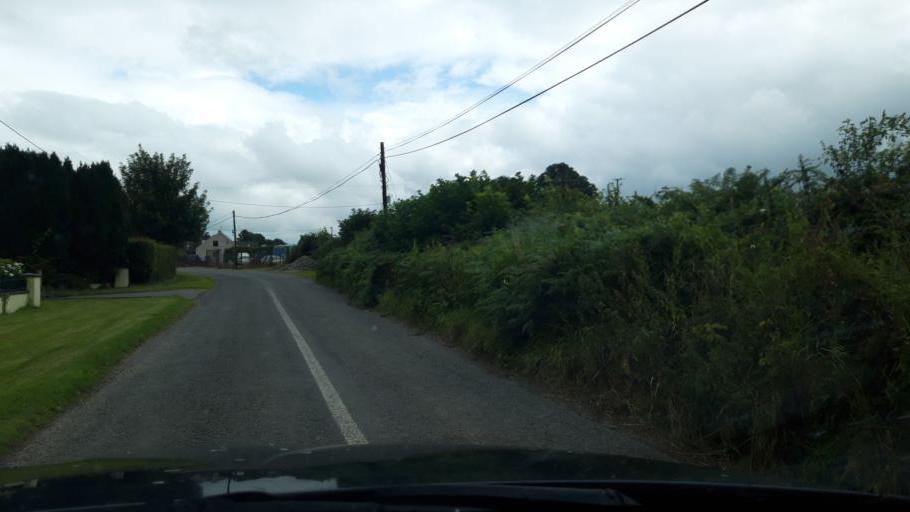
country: IE
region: Munster
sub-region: County Cork
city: Castlemartyr
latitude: 52.1354
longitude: -8.0206
